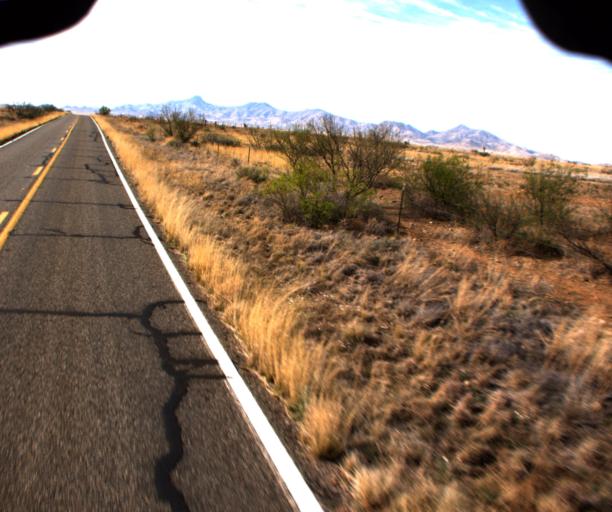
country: US
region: Arizona
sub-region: Cochise County
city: Willcox
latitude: 32.0492
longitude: -109.4901
